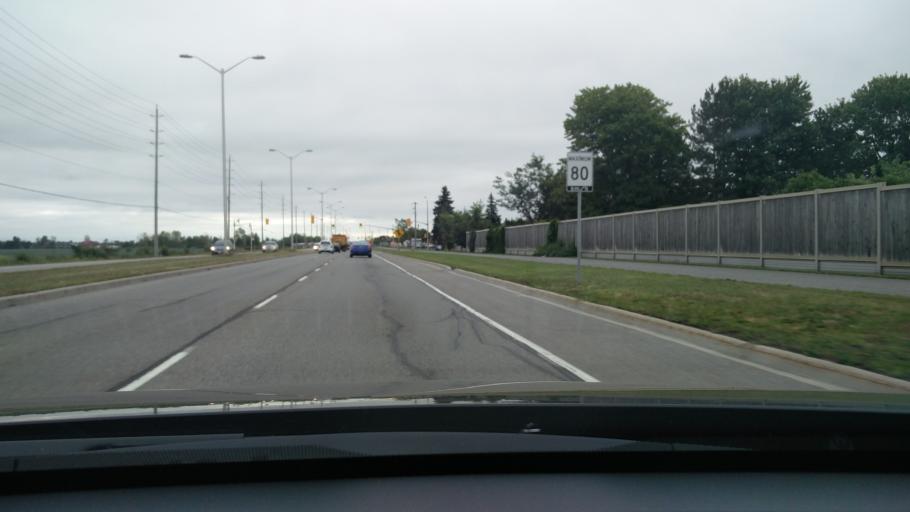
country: CA
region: Ontario
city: Bells Corners
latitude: 45.2930
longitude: -75.7451
